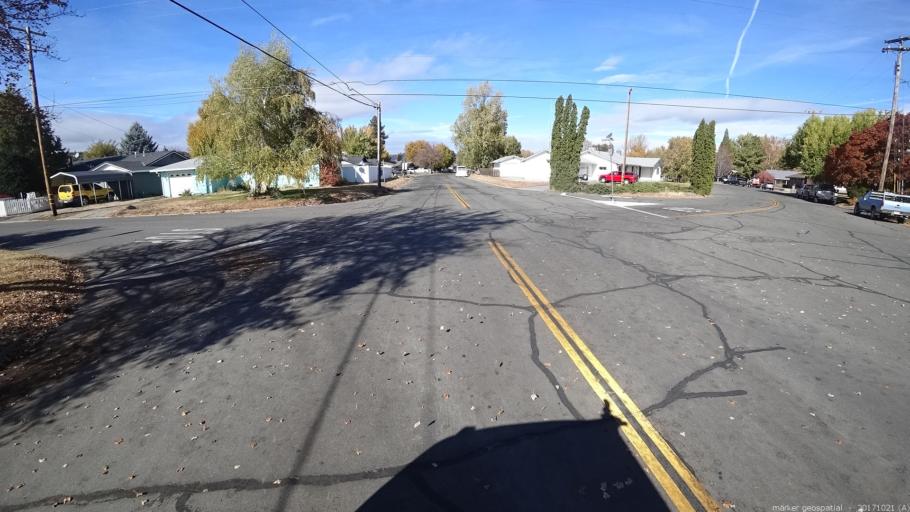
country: US
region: California
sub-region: Shasta County
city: Burney
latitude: 40.8840
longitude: -121.6621
